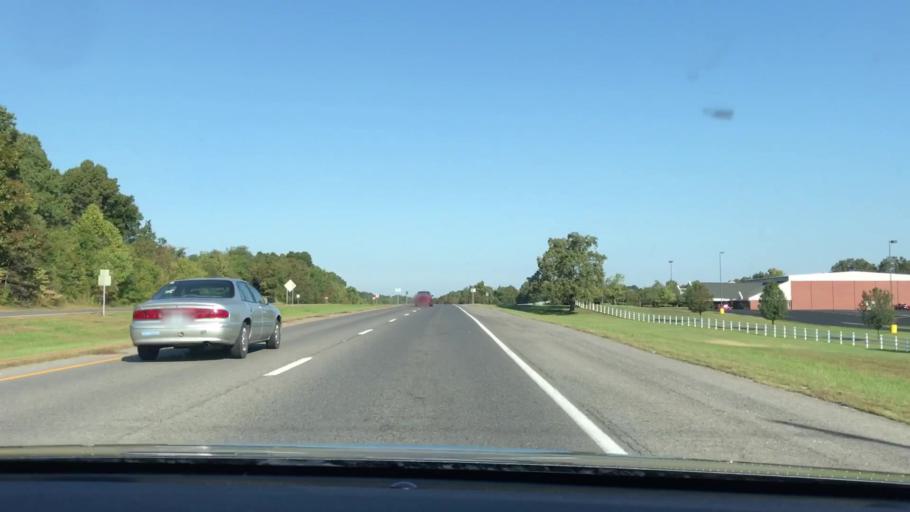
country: US
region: Kentucky
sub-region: Marshall County
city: Benton
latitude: 36.7677
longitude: -88.3126
